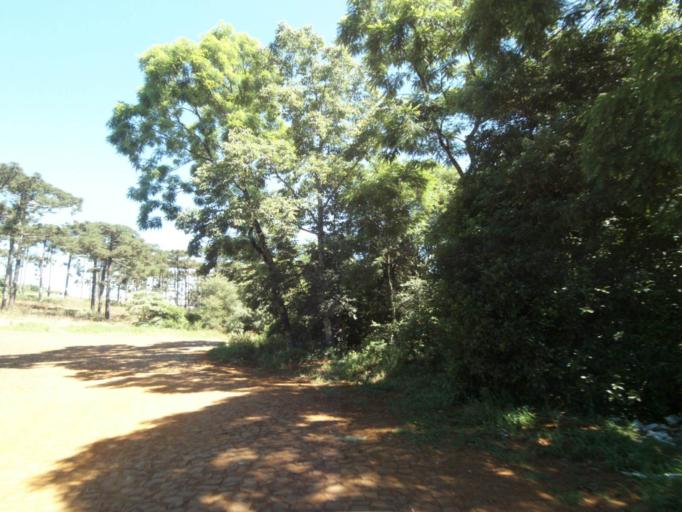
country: BR
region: Santa Catarina
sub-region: Sao Lourenco Do Oeste
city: Sao Lourenco dOeste
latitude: -26.2702
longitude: -52.7787
